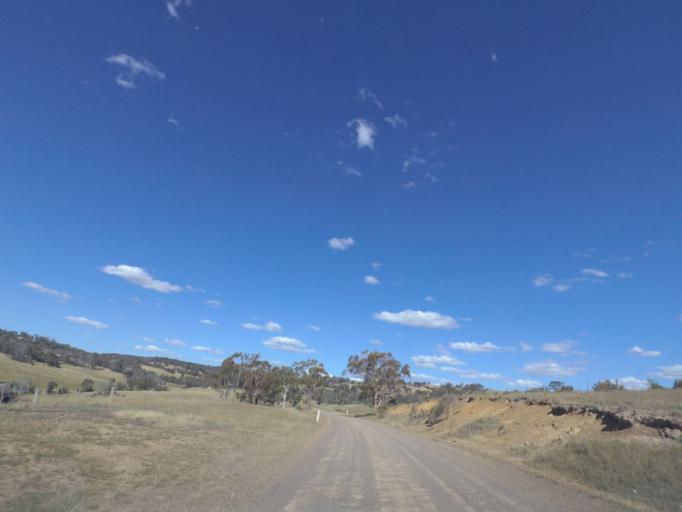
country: AU
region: Victoria
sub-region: Hume
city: Craigieburn
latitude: -37.4129
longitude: 144.9123
